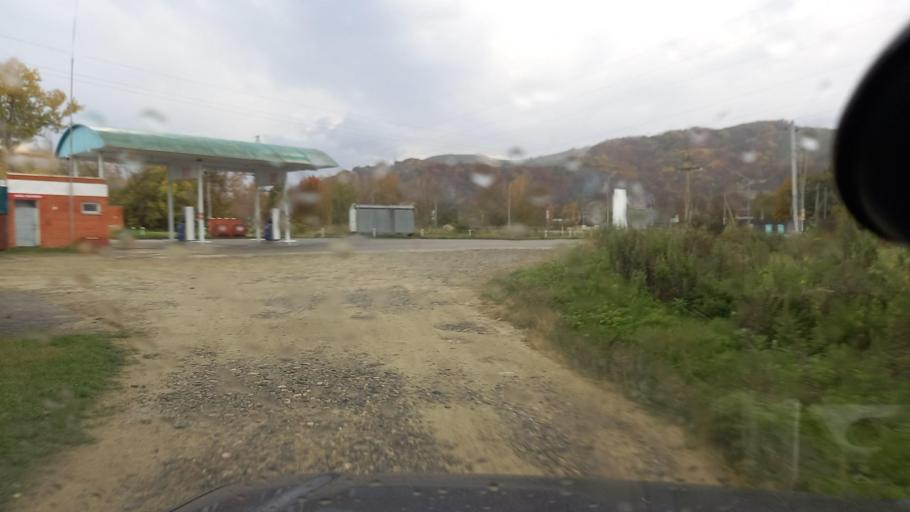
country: RU
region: Krasnodarskiy
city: Shedok
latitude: 44.1726
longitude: 40.8424
